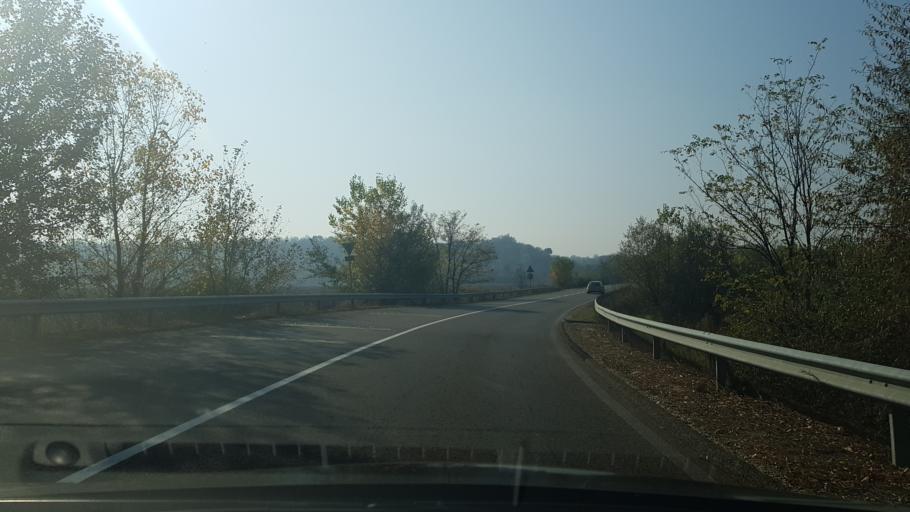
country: HU
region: Fejer
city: Adony
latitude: 47.0880
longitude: 18.8534
